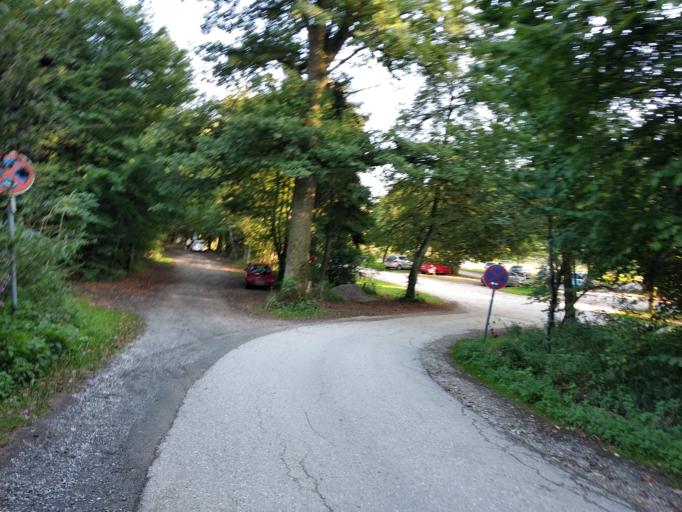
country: DE
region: Bavaria
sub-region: Upper Bavaria
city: Seeon-Seebruck
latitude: 47.9890
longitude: 12.4421
